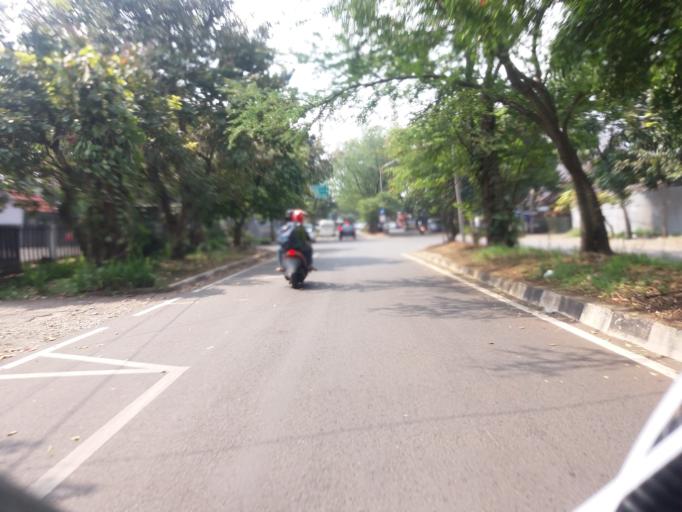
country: ID
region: West Java
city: Bandung
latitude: -6.9049
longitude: 107.6273
